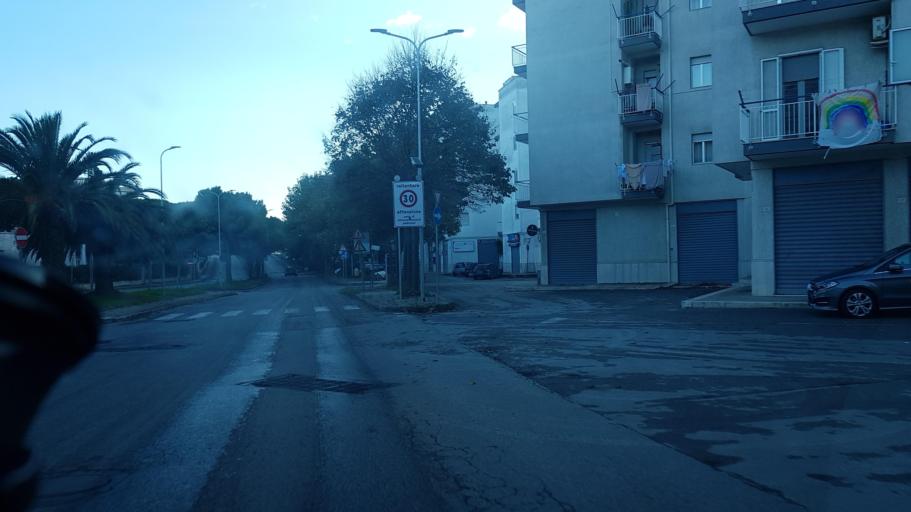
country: IT
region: Apulia
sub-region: Provincia di Brindisi
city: Ostuni
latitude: 40.7277
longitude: 17.5704
